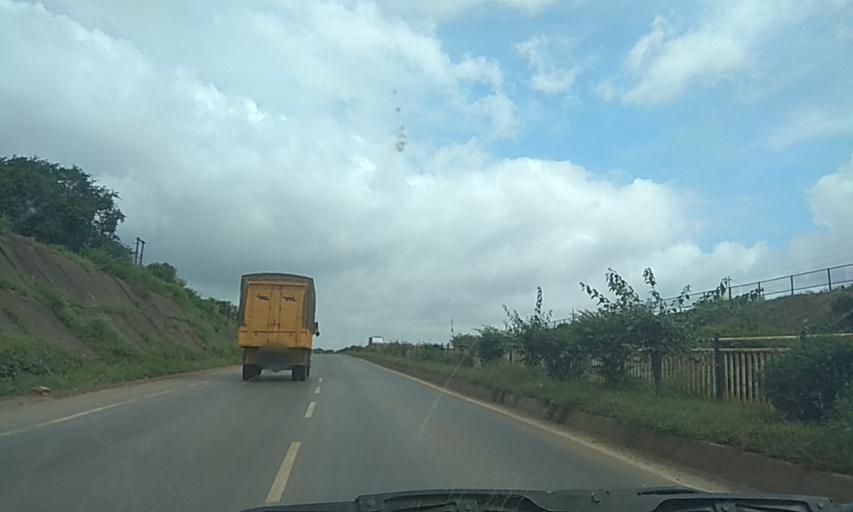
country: IN
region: Karnataka
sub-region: Dharwad
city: Kundgol
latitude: 15.2232
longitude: 75.1406
